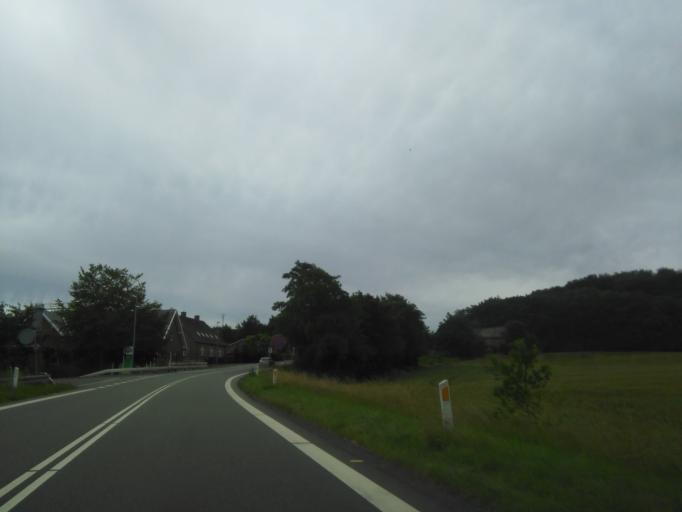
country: DK
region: Central Jutland
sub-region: Skanderborg Kommune
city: Stilling
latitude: 55.9900
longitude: 10.0231
